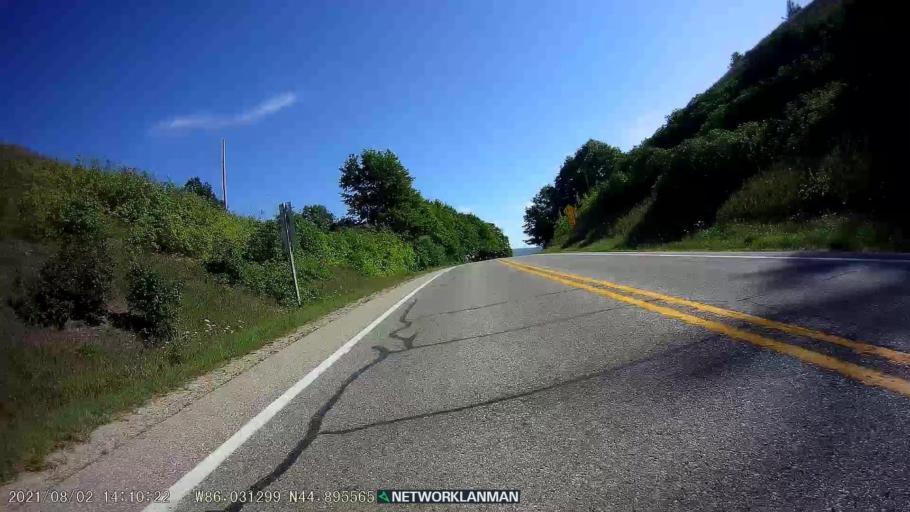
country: US
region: Michigan
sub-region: Benzie County
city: Beulah
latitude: 44.8957
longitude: -86.0314
